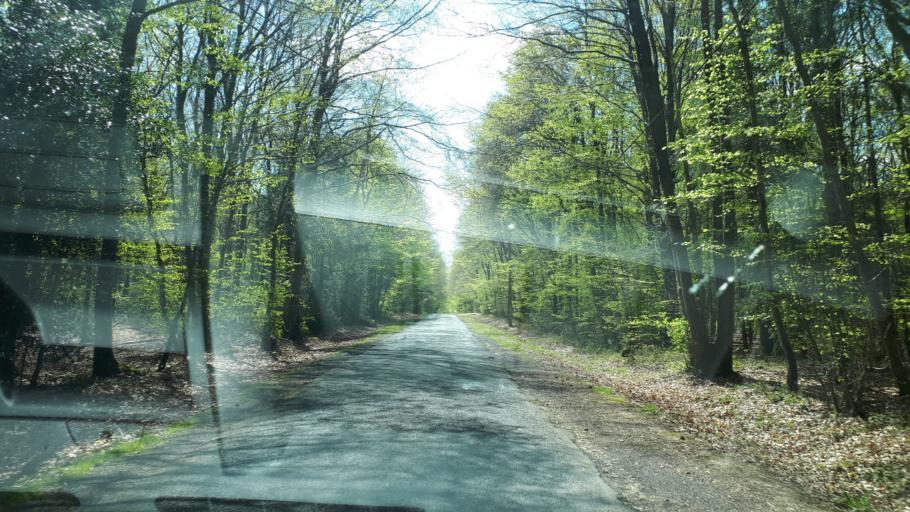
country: FR
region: Centre
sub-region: Departement du Cher
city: Henrichemont
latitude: 47.2947
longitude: 2.5791
